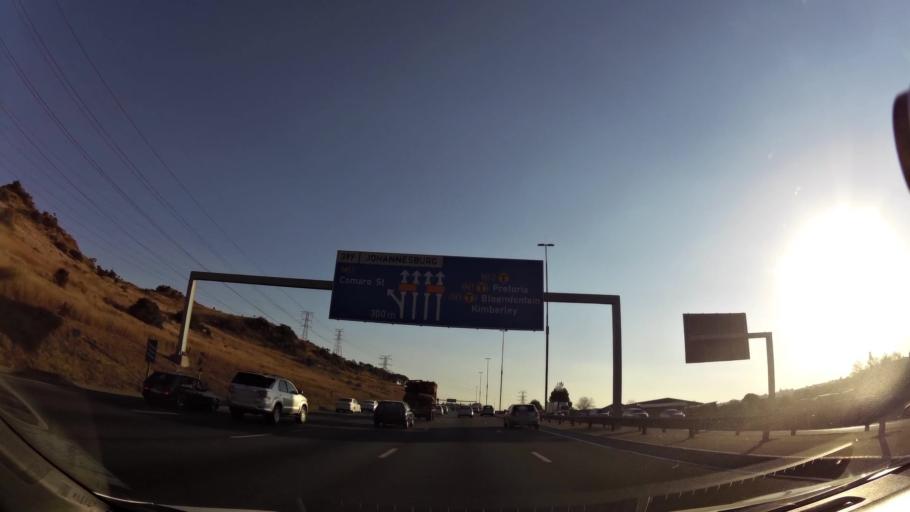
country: ZA
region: Gauteng
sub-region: City of Johannesburg Metropolitan Municipality
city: Johannesburg
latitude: -26.2678
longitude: 28.0687
